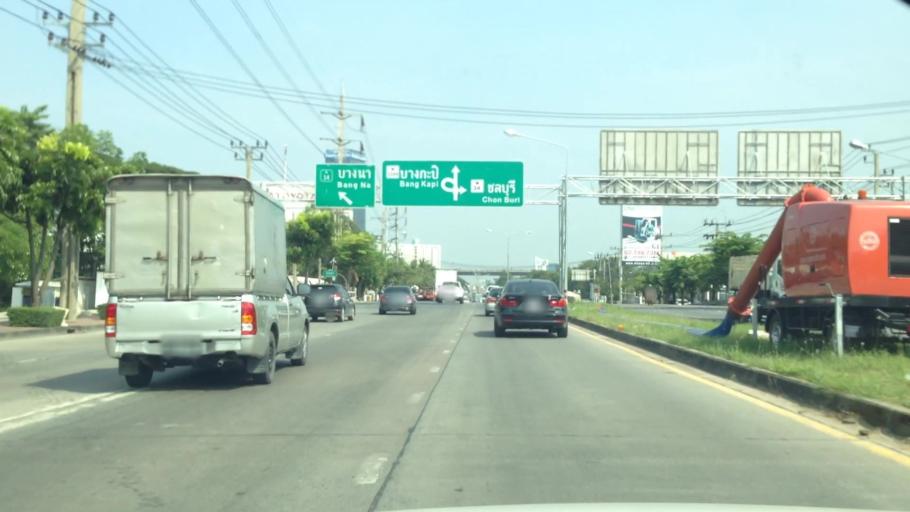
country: TH
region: Bangkok
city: Bang Na
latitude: 13.6594
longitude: 100.6430
